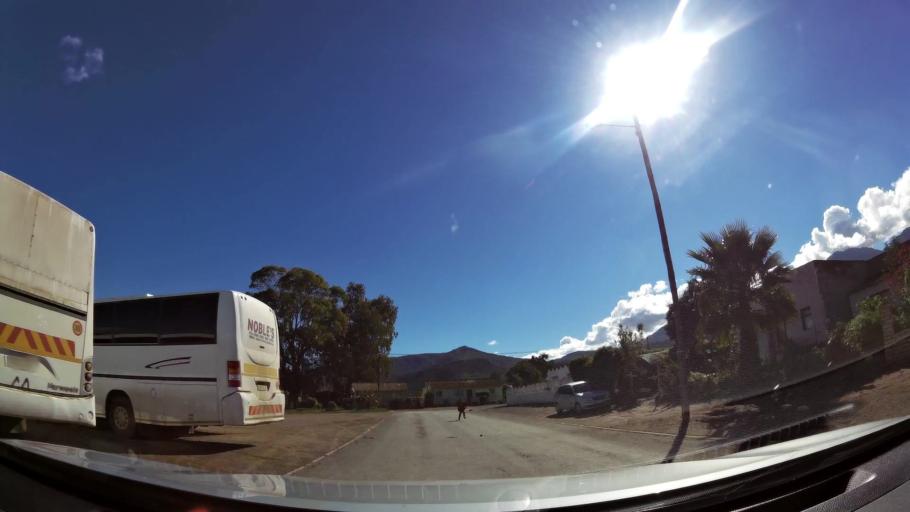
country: ZA
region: Western Cape
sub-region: Cape Winelands District Municipality
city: Ashton
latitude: -33.7938
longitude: 19.8864
